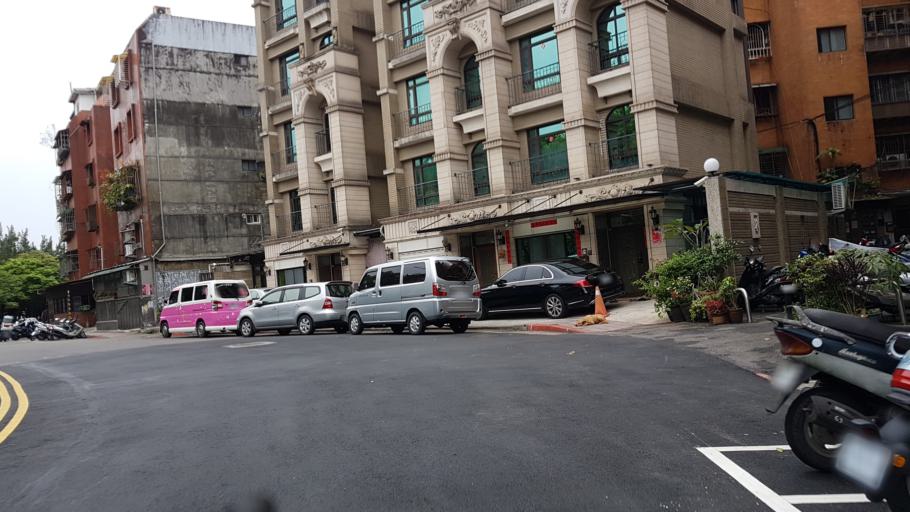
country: TW
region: Taipei
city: Taipei
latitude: 25.0442
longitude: 121.5929
